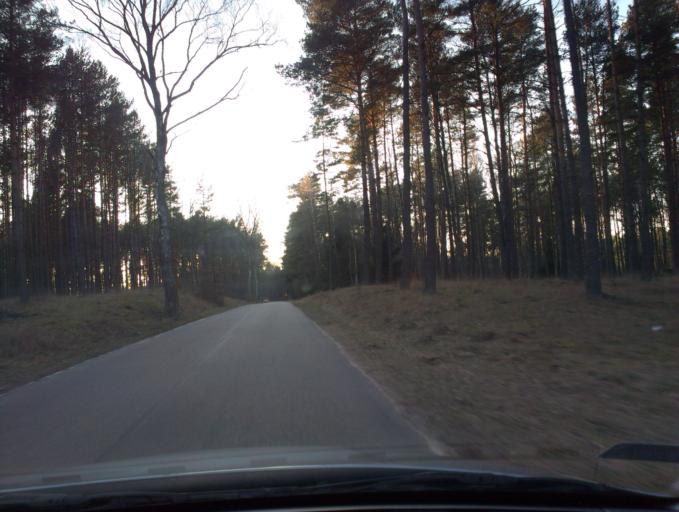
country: PL
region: West Pomeranian Voivodeship
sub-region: Powiat szczecinecki
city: Lubowo
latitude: 53.6236
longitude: 16.3699
